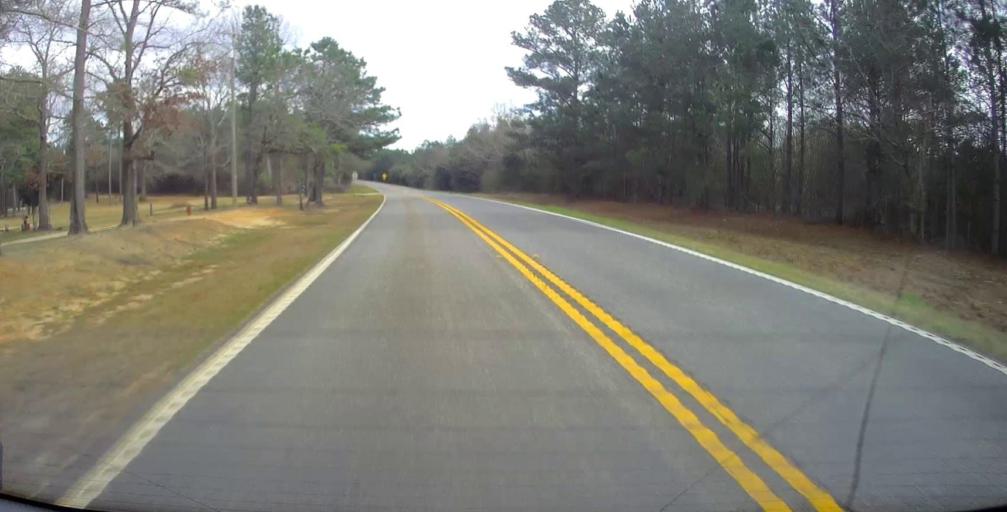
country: US
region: Georgia
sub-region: Marion County
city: Buena Vista
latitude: 32.4361
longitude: -84.4327
